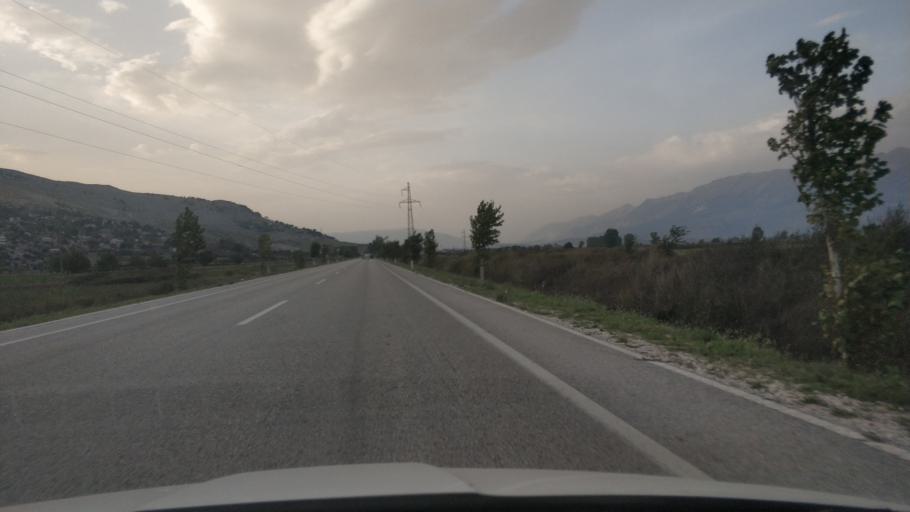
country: AL
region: Gjirokaster
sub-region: Rrethi i Gjirokastres
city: Libohove
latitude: 39.9594
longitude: 20.2465
